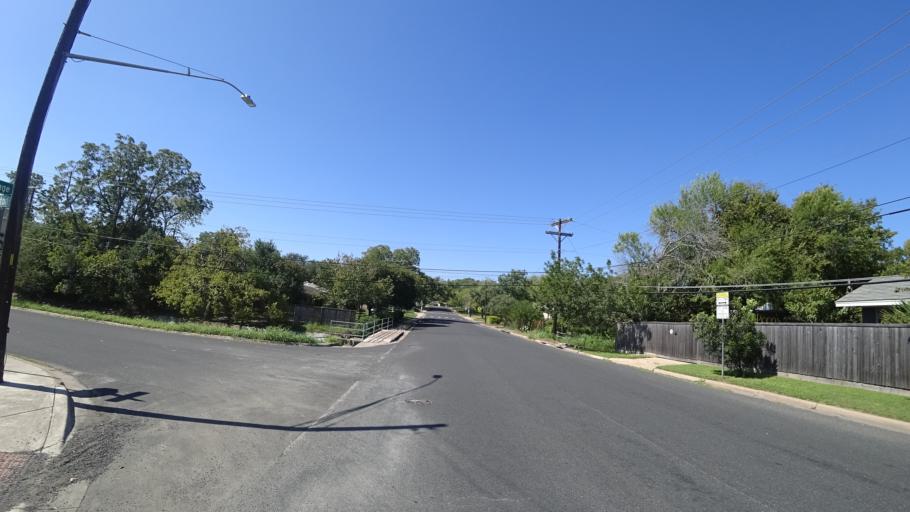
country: US
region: Texas
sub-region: Travis County
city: Austin
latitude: 30.3073
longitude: -97.6919
